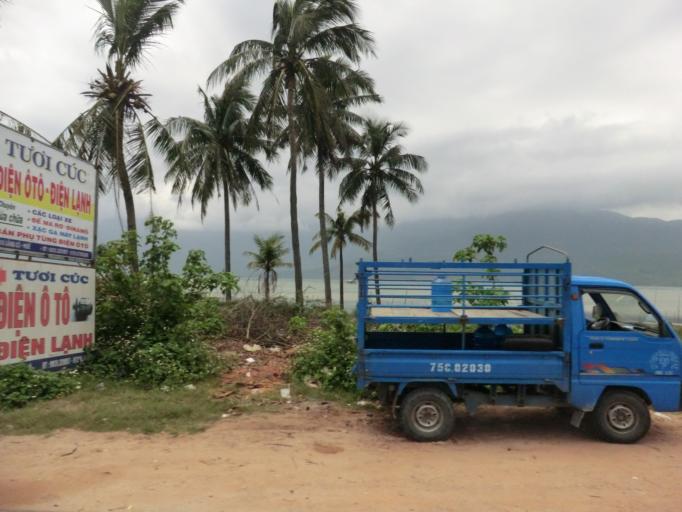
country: VN
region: Thua Thien-Hue
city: Phu Loc
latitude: 16.2598
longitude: 108.0599
